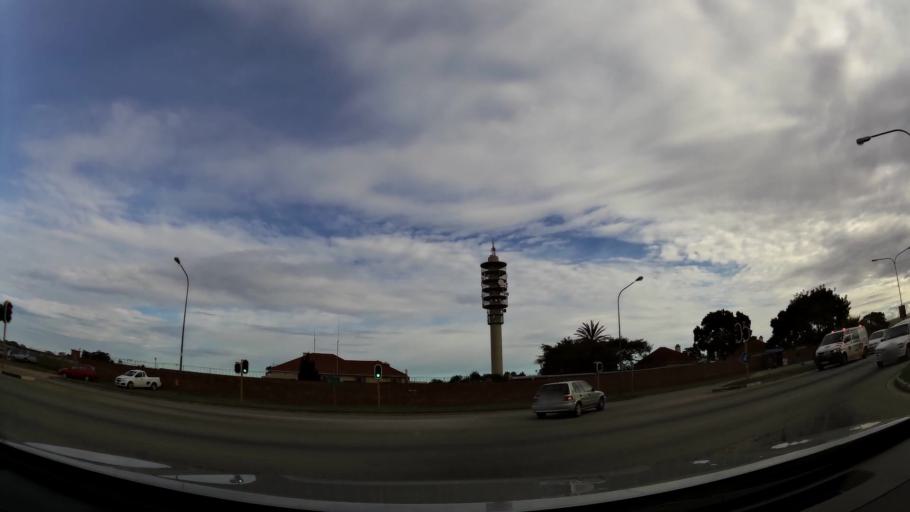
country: ZA
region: Eastern Cape
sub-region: Nelson Mandela Bay Metropolitan Municipality
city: Port Elizabeth
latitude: -33.9439
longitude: 25.5142
